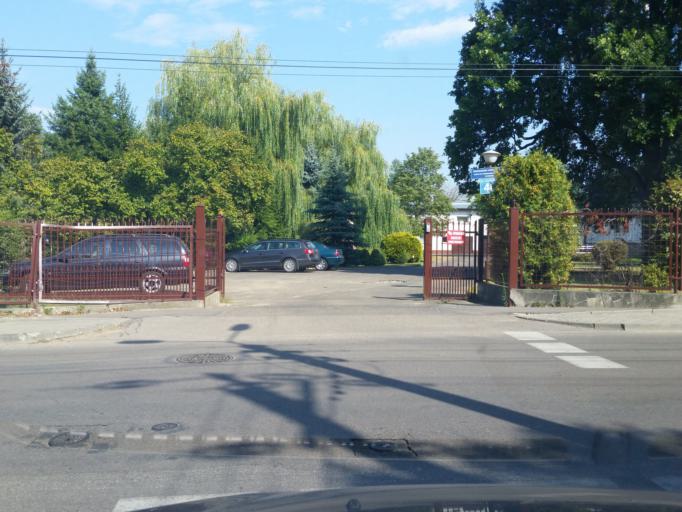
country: PL
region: Masovian Voivodeship
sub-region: Warszawa
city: Bialoleka
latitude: 52.3245
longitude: 20.9779
